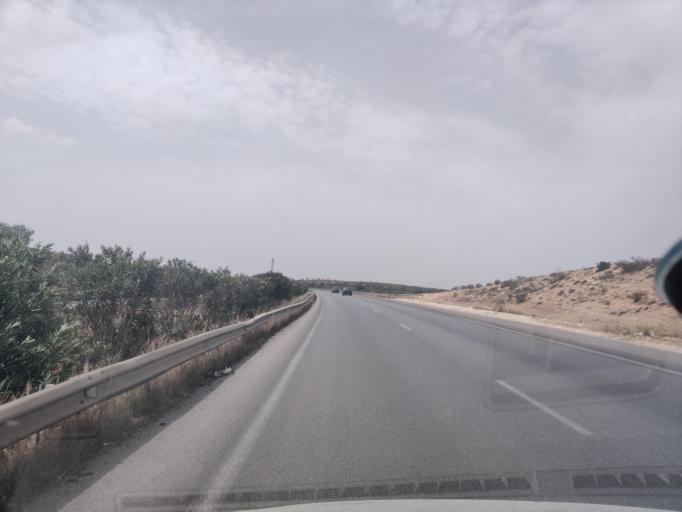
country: TN
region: Susah
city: Sidi Bou Ali
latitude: 35.9592
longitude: 10.4973
